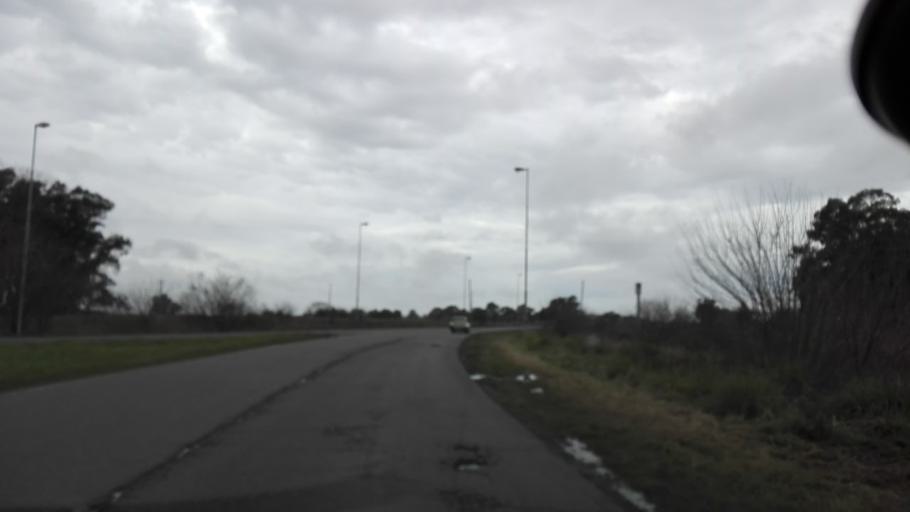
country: AR
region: Buenos Aires
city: San Miguel del Monte
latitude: -35.4314
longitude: -58.7881
